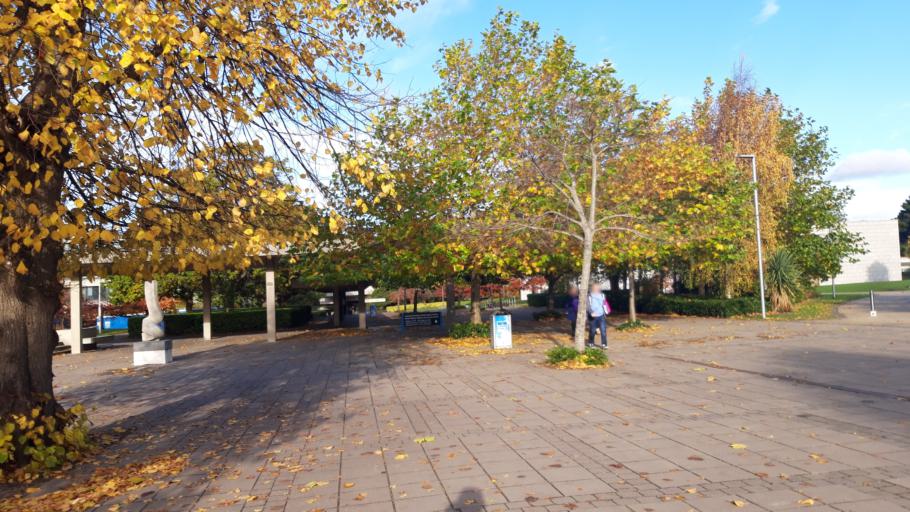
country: IE
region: Leinster
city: Mount Merrion
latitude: 53.3055
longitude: -6.2200
